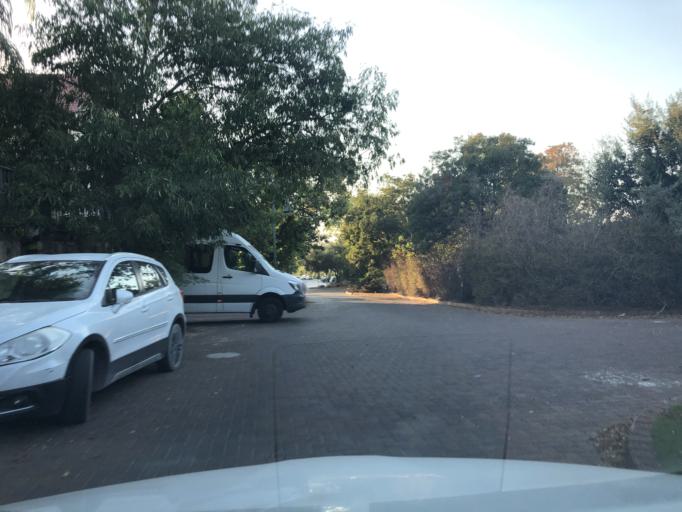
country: PS
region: West Bank
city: Hablah
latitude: 32.1626
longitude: 34.9736
